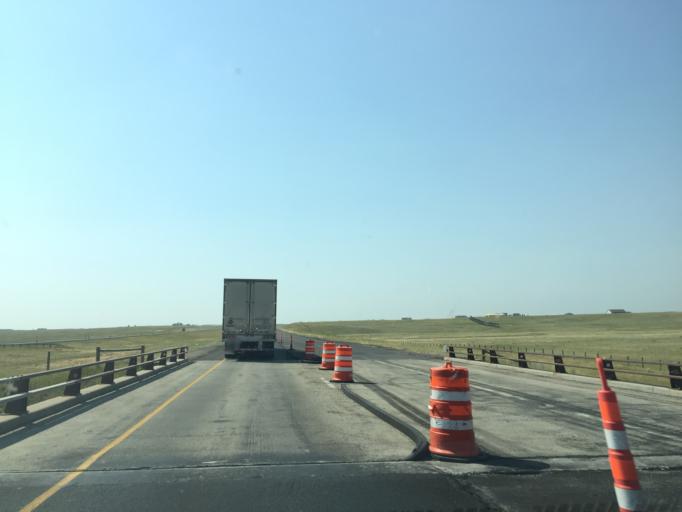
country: US
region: Wyoming
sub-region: Laramie County
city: Ranchettes
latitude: 41.3110
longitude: -104.8578
